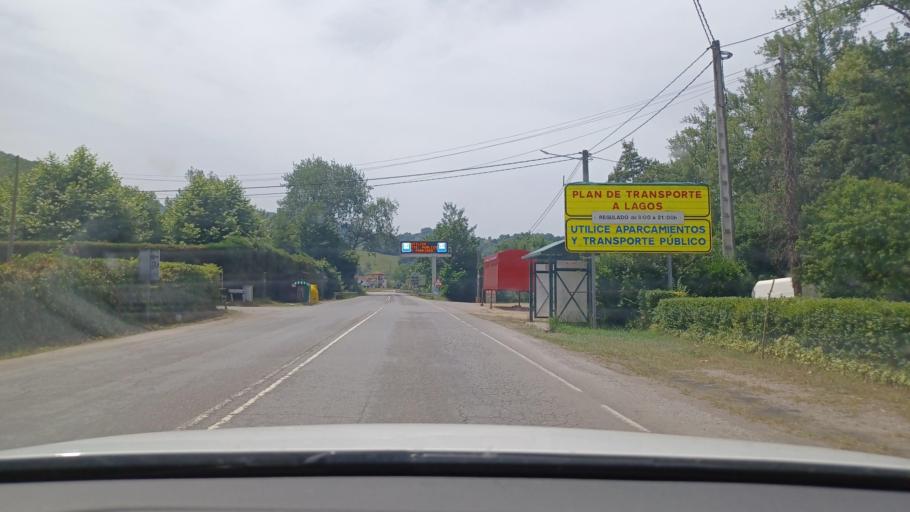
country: ES
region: Asturias
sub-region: Province of Asturias
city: Cangas de Onis
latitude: 43.3478
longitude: -5.0831
